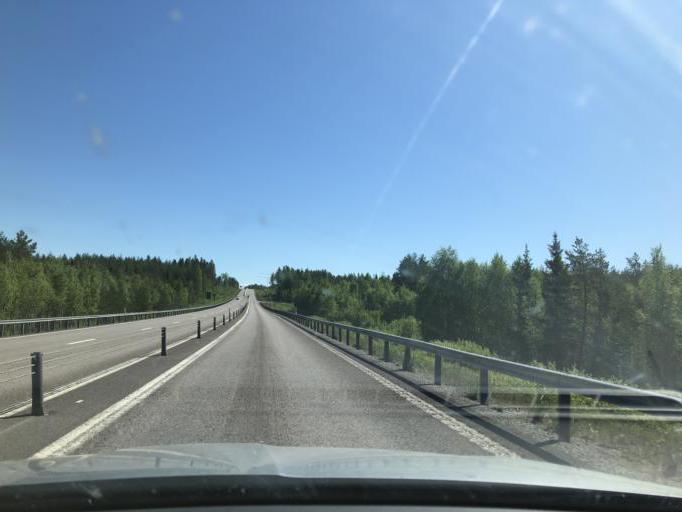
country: SE
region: Norrbotten
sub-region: Kalix Kommun
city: Toere
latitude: 65.9123
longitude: 22.8008
